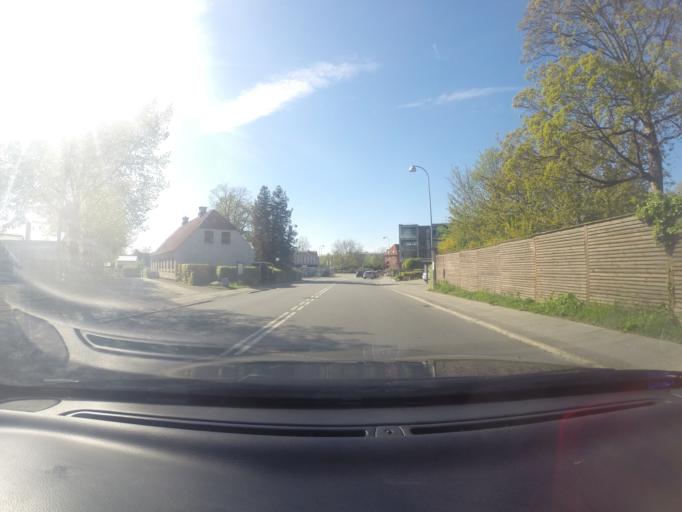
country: DK
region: Capital Region
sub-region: Gladsaxe Municipality
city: Buddinge
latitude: 55.7587
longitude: 12.4542
